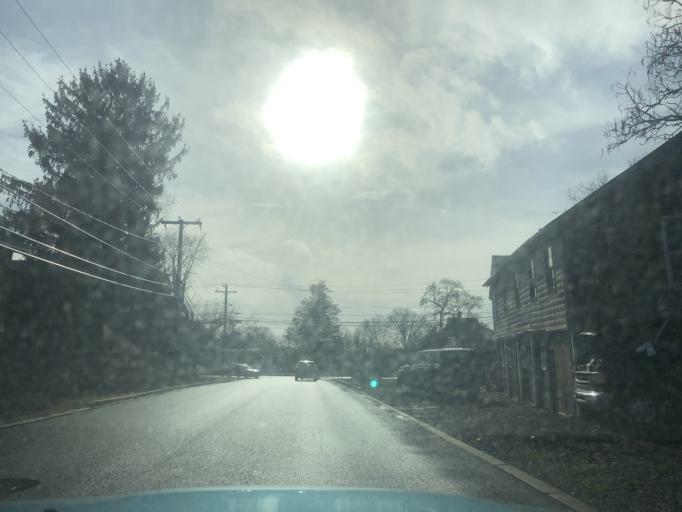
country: US
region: Pennsylvania
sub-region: Bucks County
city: Quakertown
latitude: 40.4484
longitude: -75.3341
